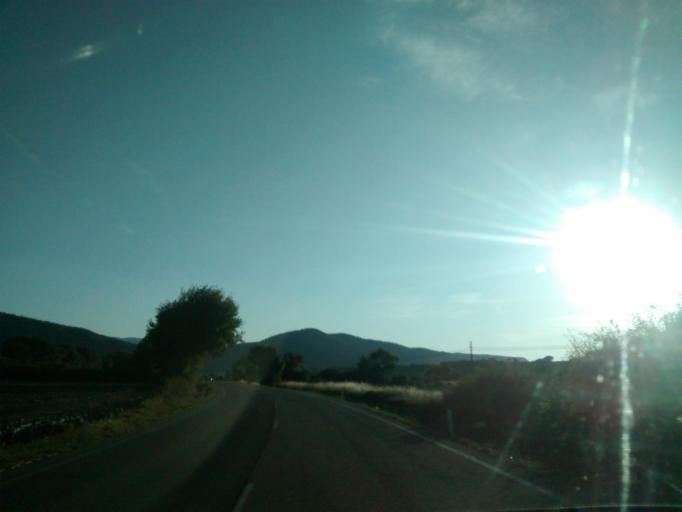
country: ES
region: Aragon
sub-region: Provincia de Huesca
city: Bailo
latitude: 42.5709
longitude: -0.7707
